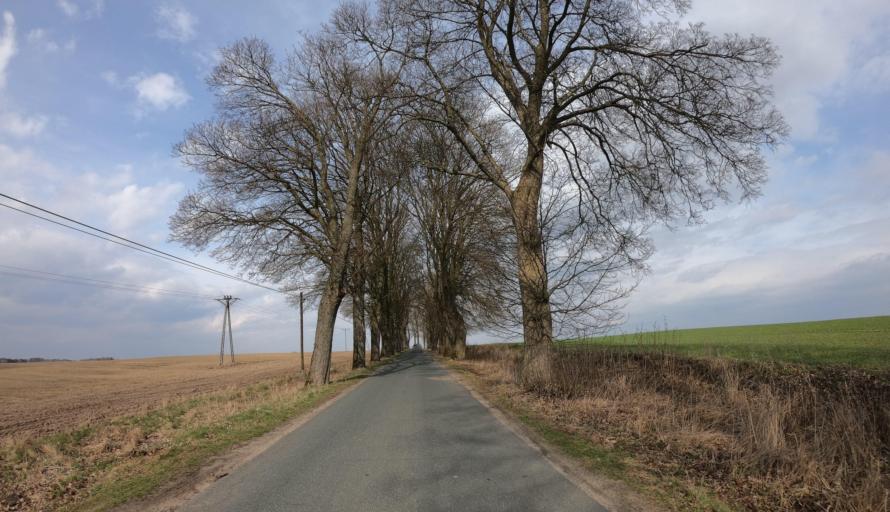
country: PL
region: West Pomeranian Voivodeship
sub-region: Powiat swidwinski
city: Swidwin
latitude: 53.8290
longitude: 15.8285
